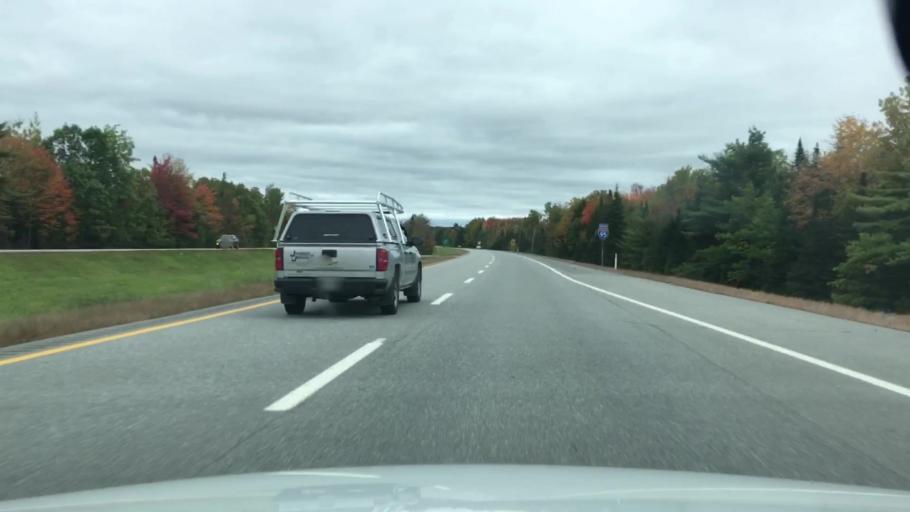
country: US
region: Maine
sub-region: Penobscot County
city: Newport
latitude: 44.8158
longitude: -69.2538
